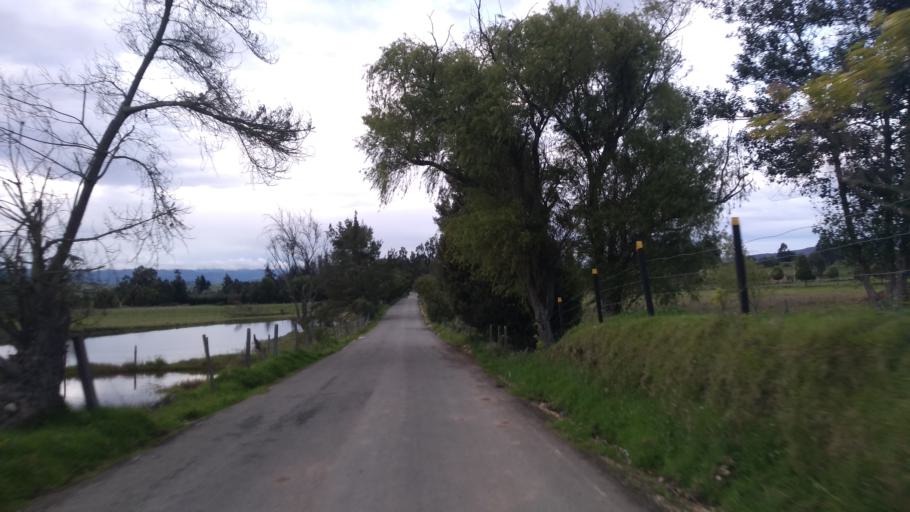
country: CO
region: Boyaca
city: Toca
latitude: 5.5833
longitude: -73.1834
